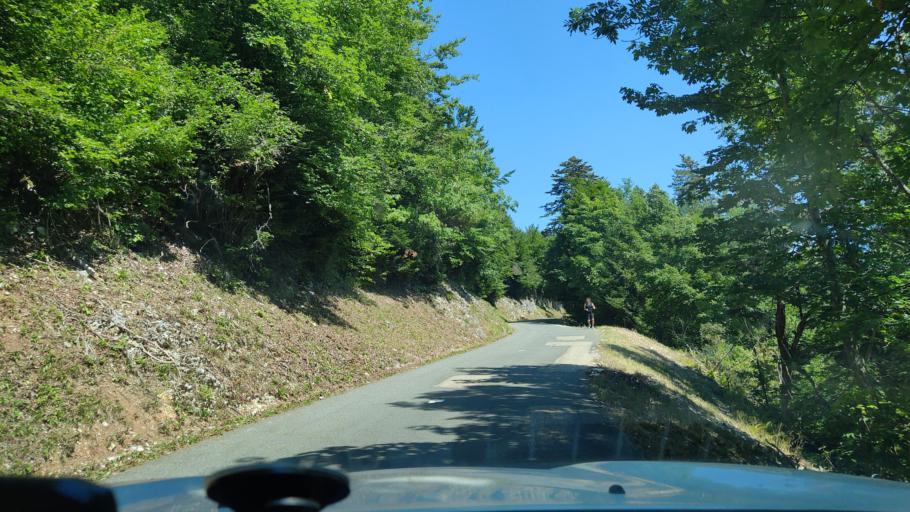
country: FR
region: Rhone-Alpes
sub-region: Departement de la Savoie
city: Le Bourget-du-Lac
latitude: 45.6513
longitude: 5.8242
